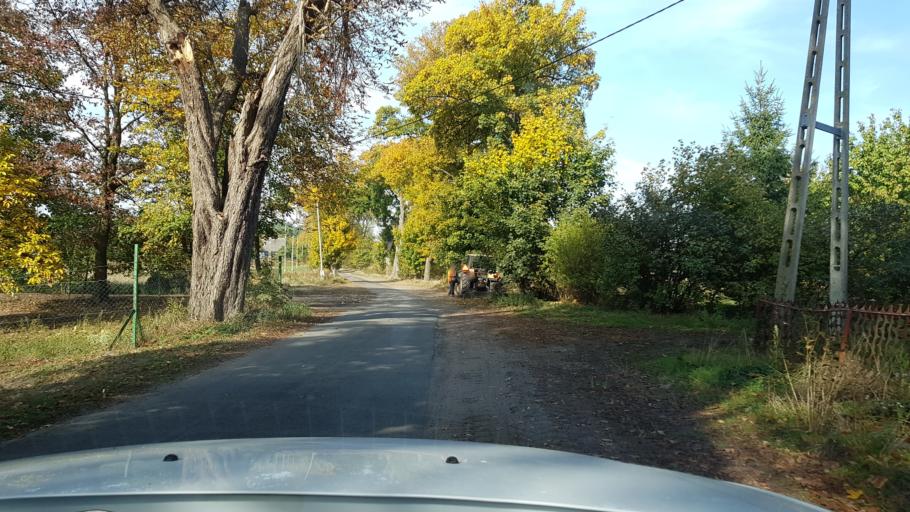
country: PL
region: West Pomeranian Voivodeship
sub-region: Powiat mysliborski
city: Mysliborz
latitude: 52.9319
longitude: 14.9405
